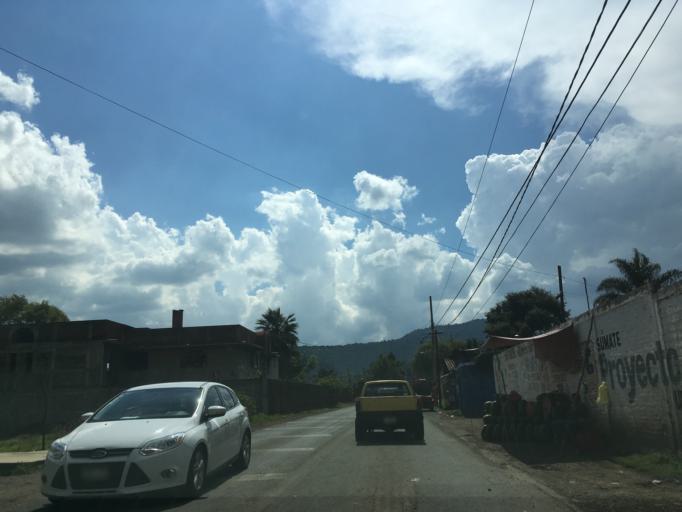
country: MX
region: Michoacan
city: Patzcuaro
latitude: 19.5331
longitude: -101.6181
